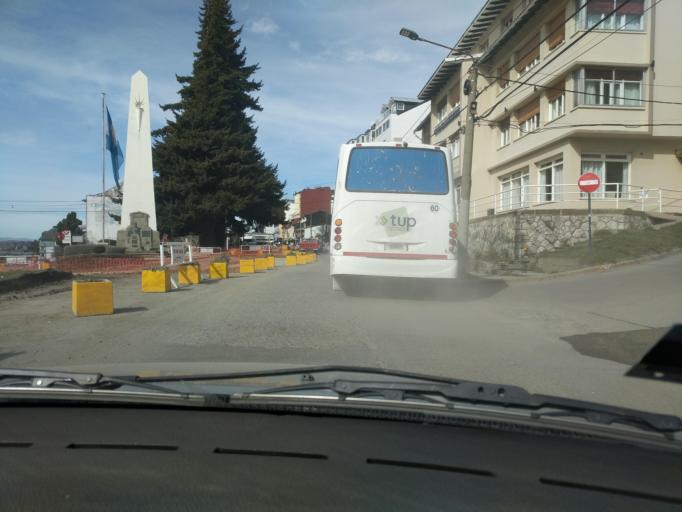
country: AR
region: Rio Negro
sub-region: Departamento de Bariloche
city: San Carlos de Bariloche
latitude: -41.1327
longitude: -71.3199
